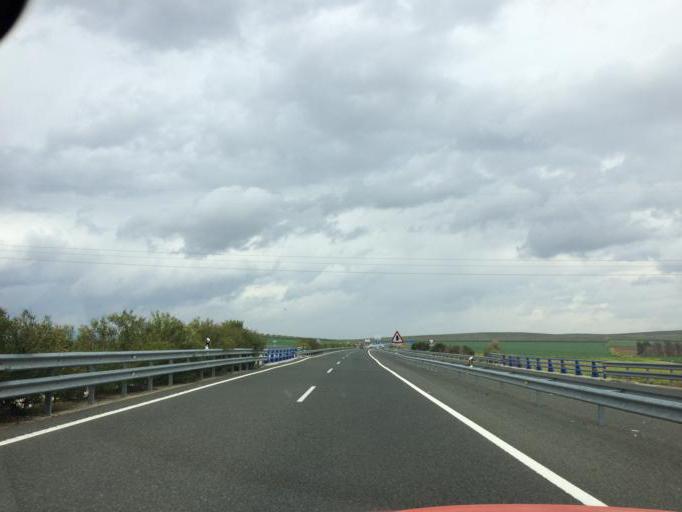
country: ES
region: Andalusia
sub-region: Provincia de Malaga
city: Antequera
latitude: 37.0718
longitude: -4.5306
